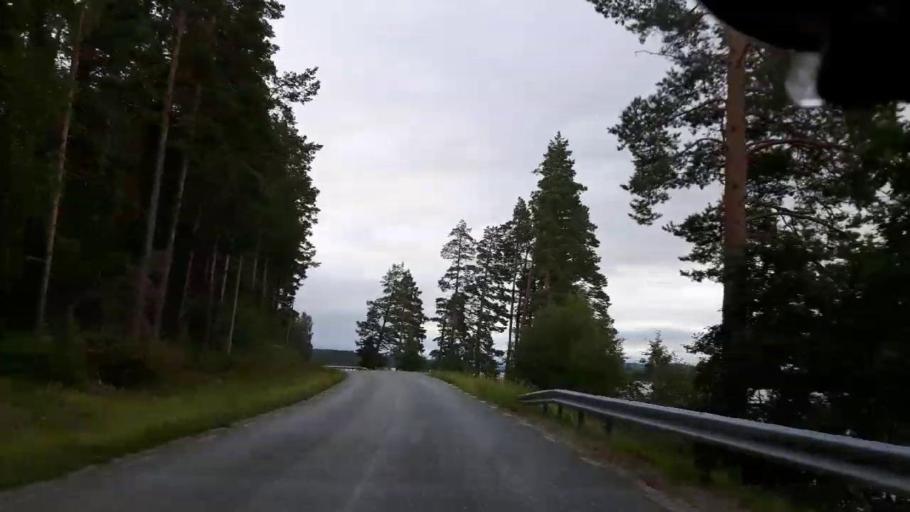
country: SE
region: Jaemtland
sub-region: Braecke Kommun
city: Braecke
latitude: 62.8634
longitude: 15.6209
